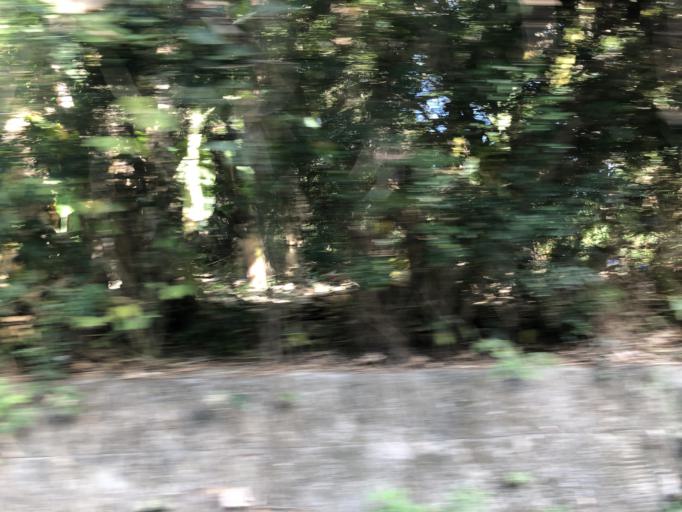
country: TW
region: Taiwan
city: Yujing
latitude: 23.0217
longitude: 120.3972
